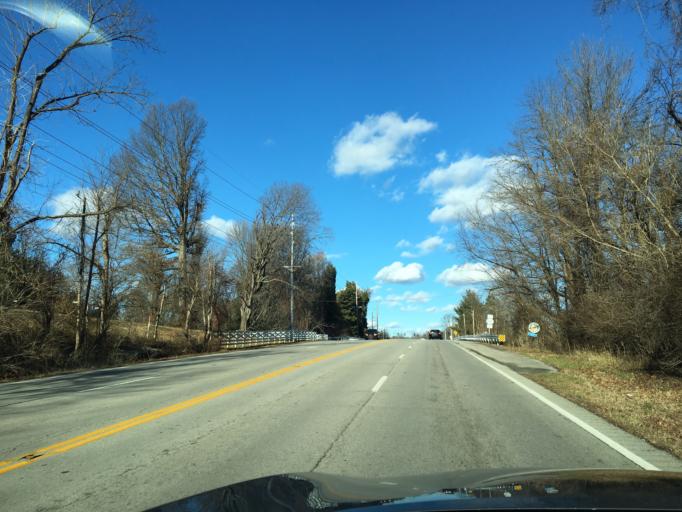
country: US
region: Kentucky
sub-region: Jefferson County
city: Prospect
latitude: 38.3192
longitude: -85.6233
